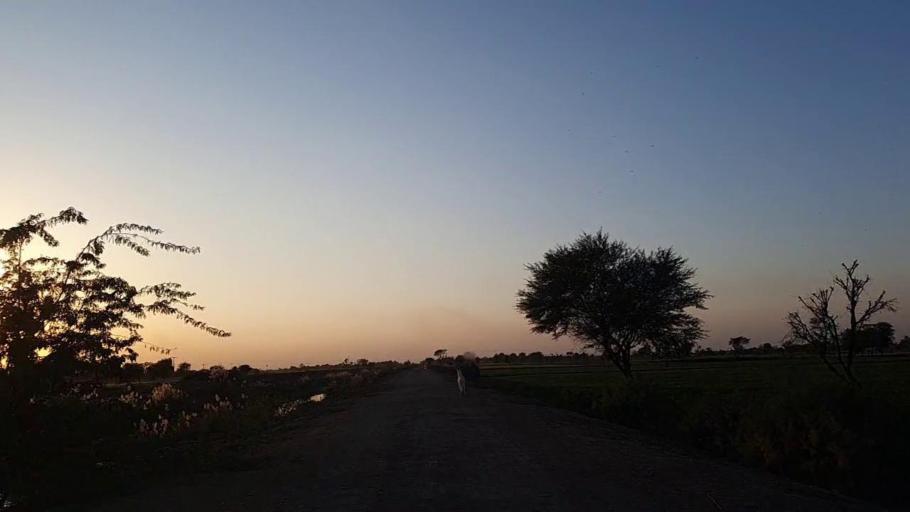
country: PK
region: Sindh
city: Jam Sahib
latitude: 26.3099
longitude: 68.6623
